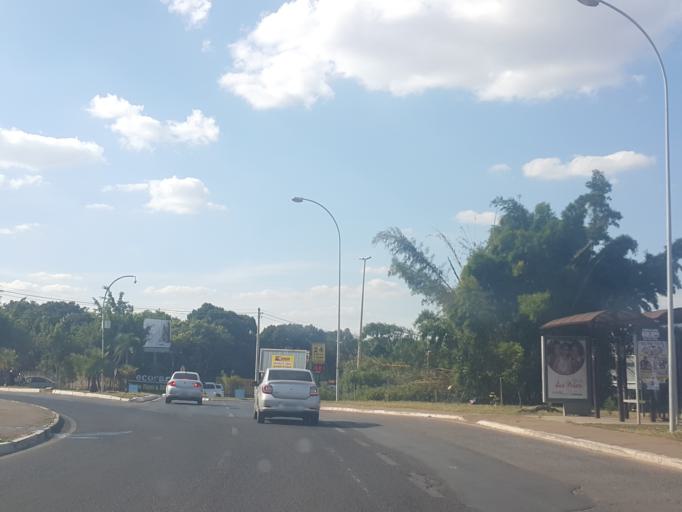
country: BR
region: Federal District
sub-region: Brasilia
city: Brasilia
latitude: -15.8361
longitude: -48.0078
